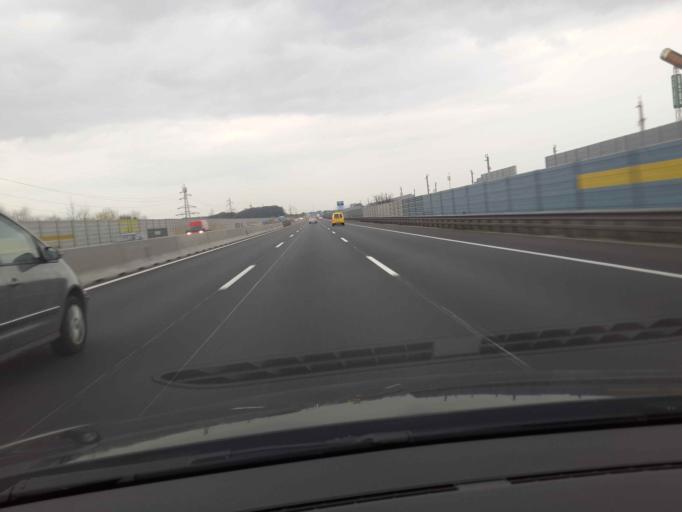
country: AT
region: Lower Austria
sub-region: Sankt Polten Stadt
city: Sankt Poelten
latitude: 48.1767
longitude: 15.6282
